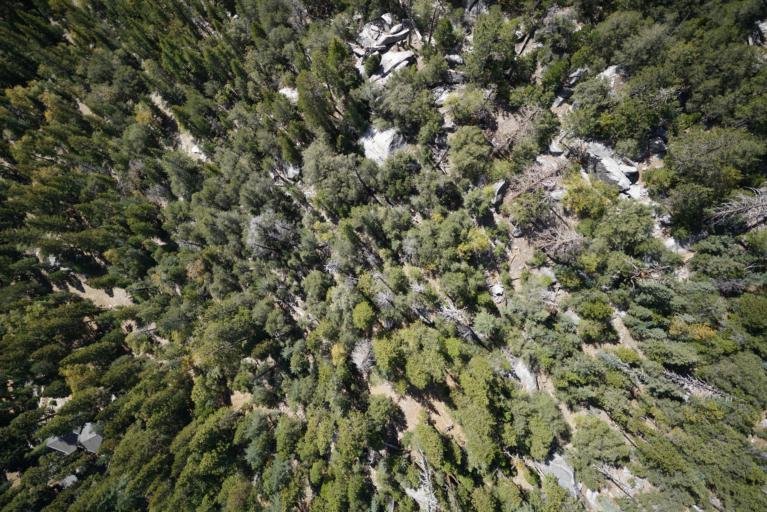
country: US
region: California
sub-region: Riverside County
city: Idyllwild
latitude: 33.7692
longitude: -116.6921
